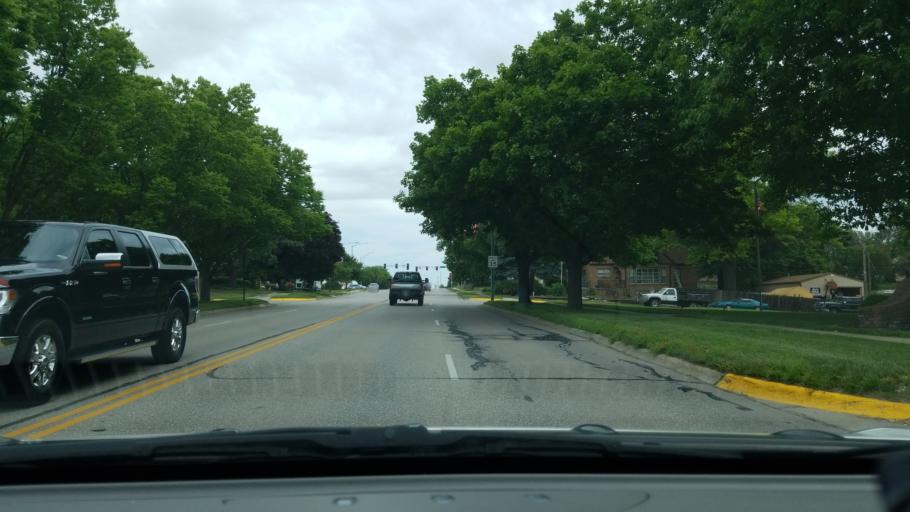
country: US
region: Nebraska
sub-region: Sarpy County
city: Papillion
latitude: 41.1599
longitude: -96.0429
